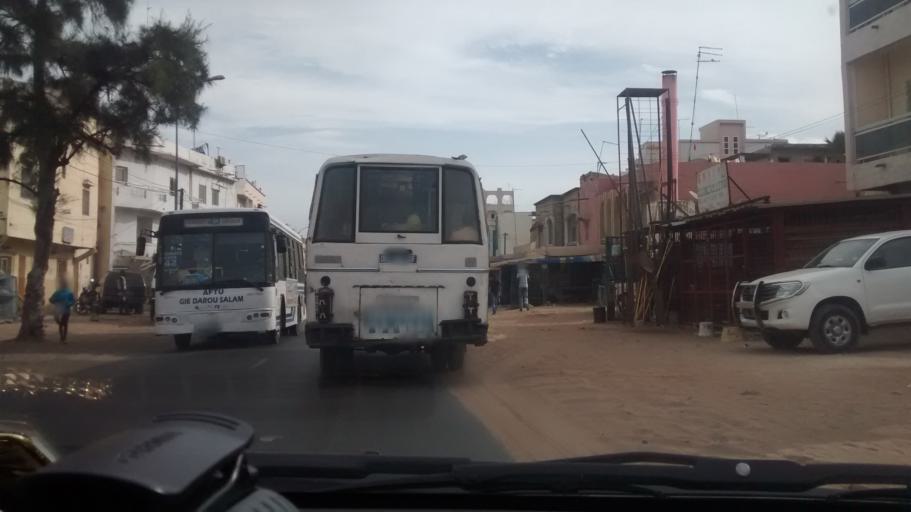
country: SN
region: Dakar
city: Pikine
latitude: 14.7659
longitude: -17.4158
